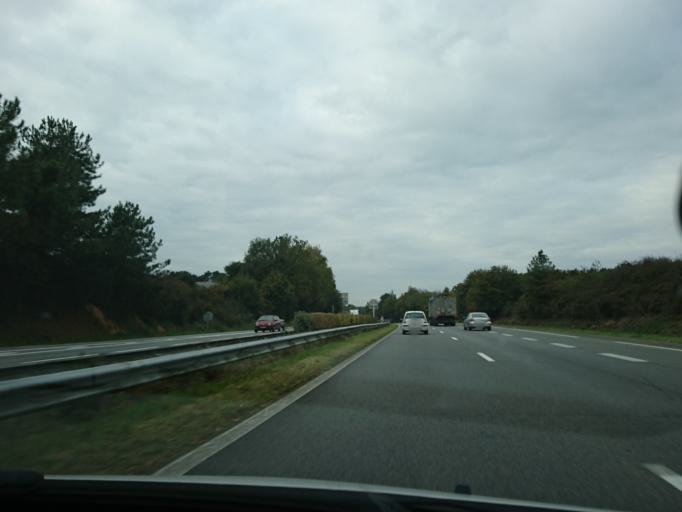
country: FR
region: Pays de la Loire
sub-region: Departement de la Loire-Atlantique
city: Missillac
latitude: 47.4787
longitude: -2.1832
